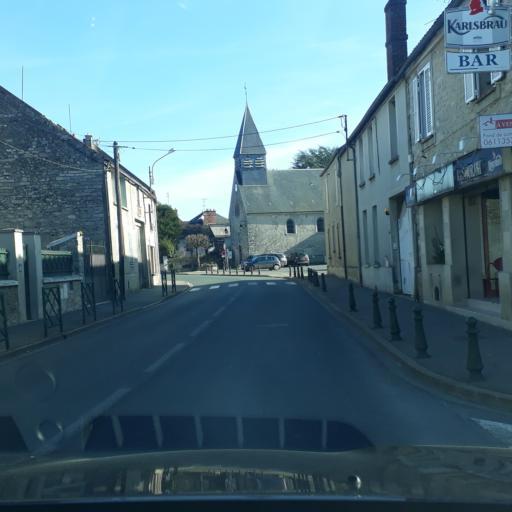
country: FR
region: Ile-de-France
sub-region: Departement de l'Essonne
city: Boissy-le-Cutte
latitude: 48.4698
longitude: 2.2825
